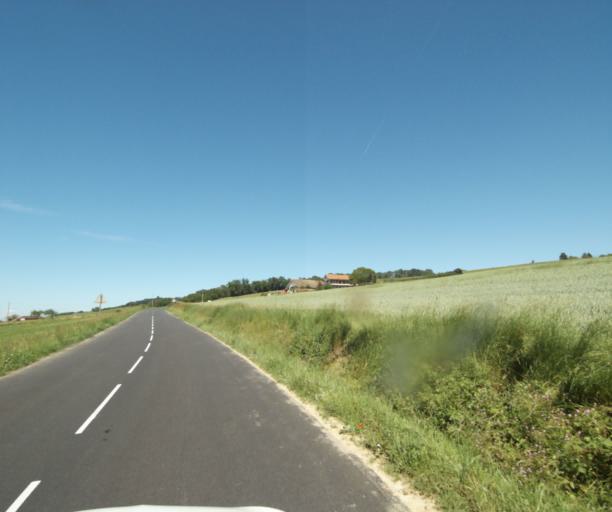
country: FR
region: Rhone-Alpes
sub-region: Departement de la Haute-Savoie
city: Loisin
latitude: 46.2889
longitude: 6.3136
